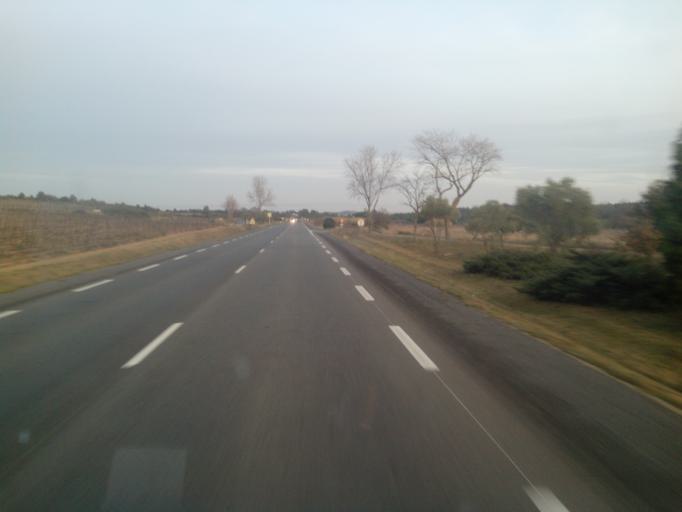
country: FR
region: Languedoc-Roussillon
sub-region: Departement de l'Herault
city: Olonzac
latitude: 43.2746
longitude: 2.7829
